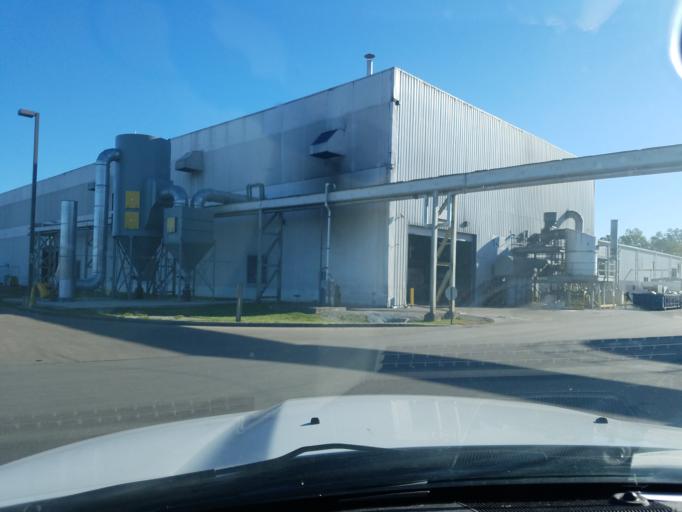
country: US
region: Kentucky
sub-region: Laurel County
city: North Corbin
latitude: 37.0351
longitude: -84.0663
